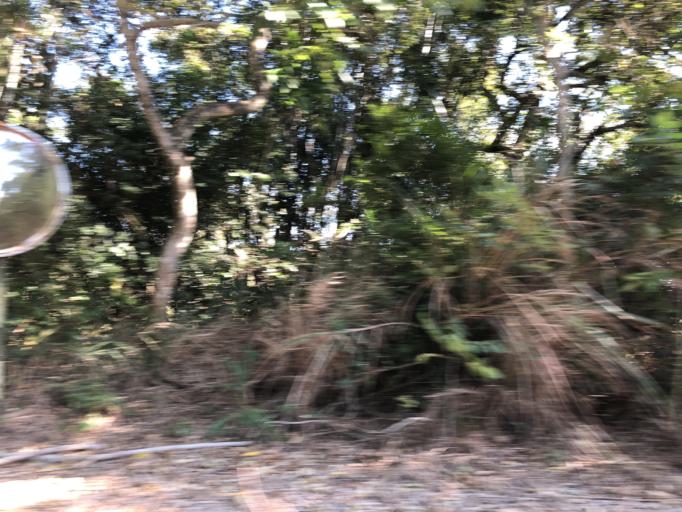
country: TW
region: Taiwan
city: Yujing
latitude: 23.0312
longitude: 120.3854
